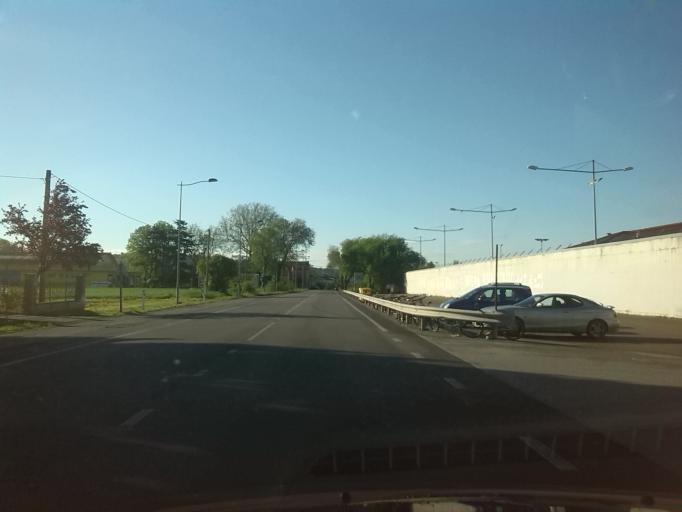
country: IT
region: Friuli Venezia Giulia
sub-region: Provincia di Gorizia
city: Sagrado
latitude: 45.8881
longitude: 13.4787
